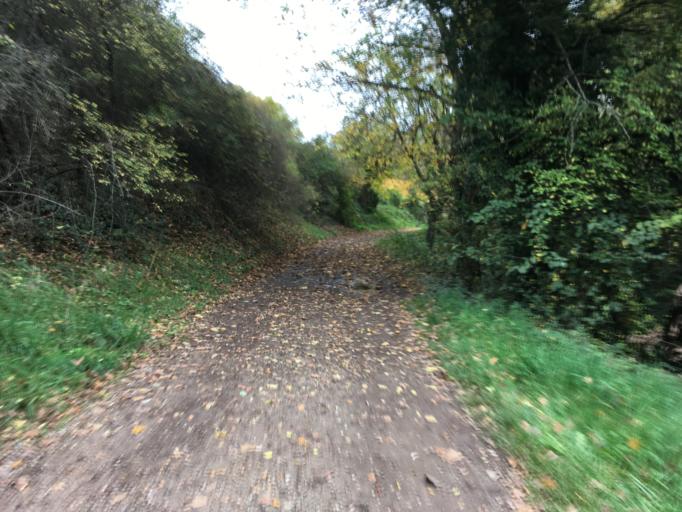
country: DE
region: Baden-Wuerttemberg
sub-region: Freiburg Region
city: Sasbach
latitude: 48.1008
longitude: 7.5935
